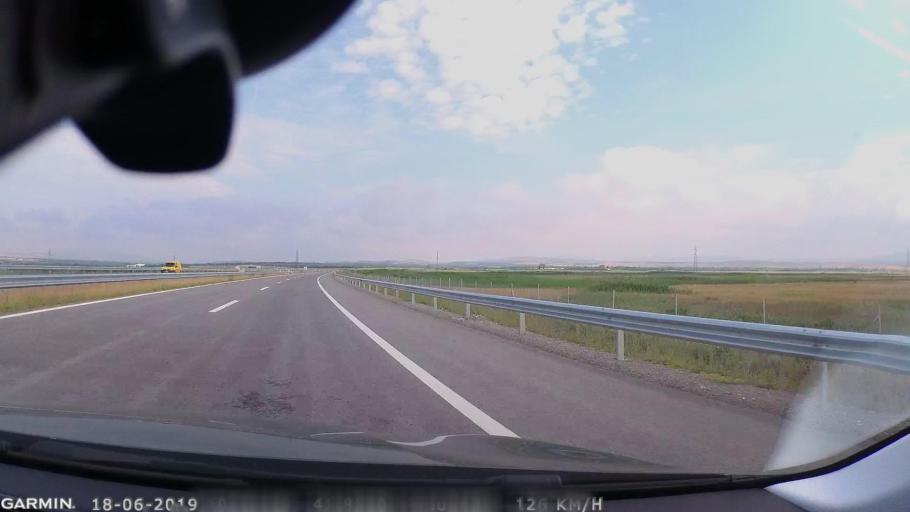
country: MK
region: Sveti Nikole
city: Sveti Nikole
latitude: 41.8184
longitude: 22.0159
